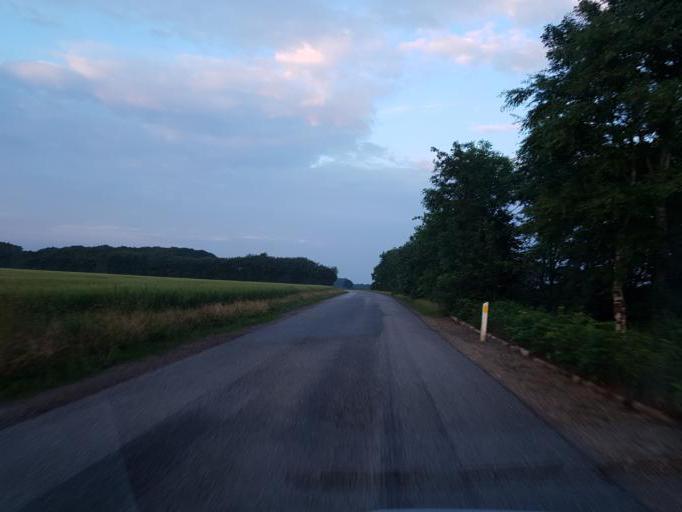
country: DK
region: South Denmark
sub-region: Esbjerg Kommune
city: Tjaereborg
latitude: 55.5126
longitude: 8.5705
